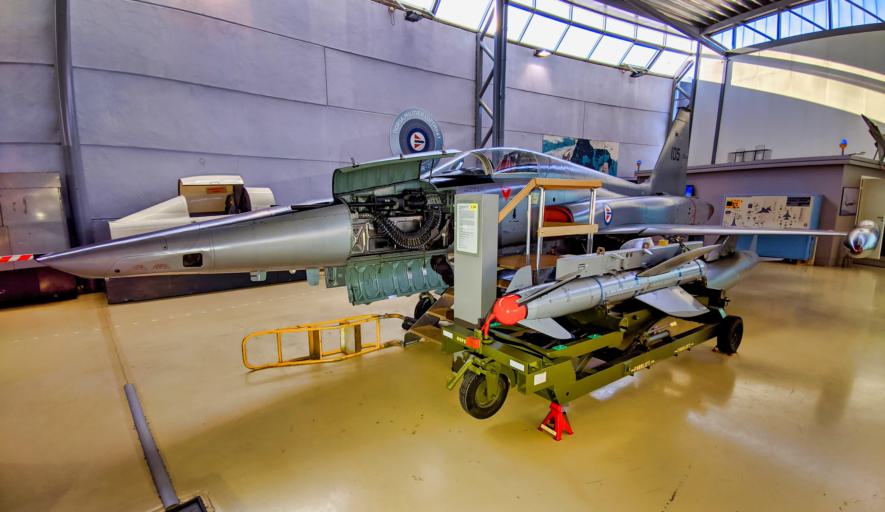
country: NO
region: Akershus
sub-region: Nannestad
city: Teigebyen
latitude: 60.1887
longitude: 11.0697
